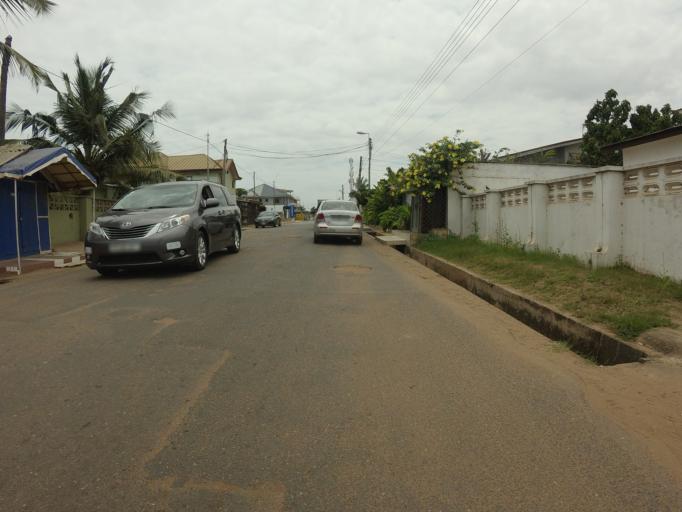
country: GH
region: Greater Accra
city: Nungua
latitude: 5.6055
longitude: -0.0996
